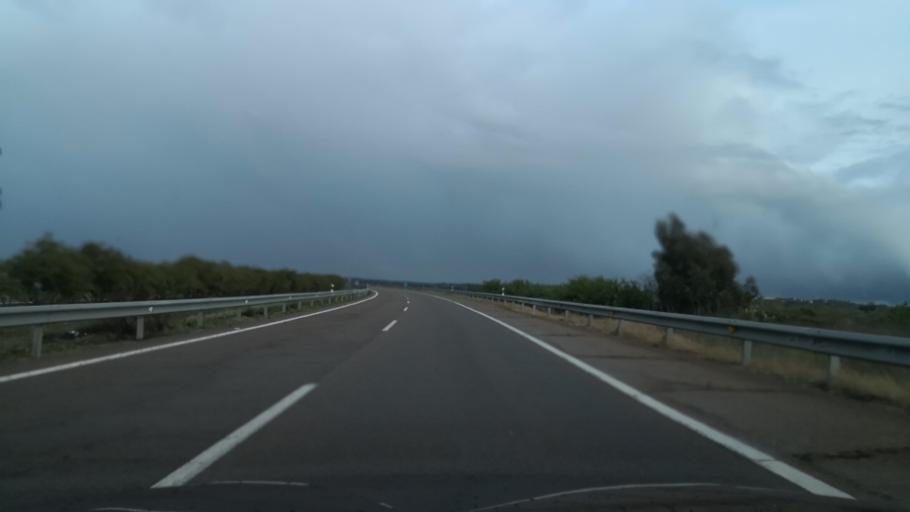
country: ES
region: Extremadura
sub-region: Provincia de Badajoz
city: Badajoz
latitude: 38.9118
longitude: -6.9482
